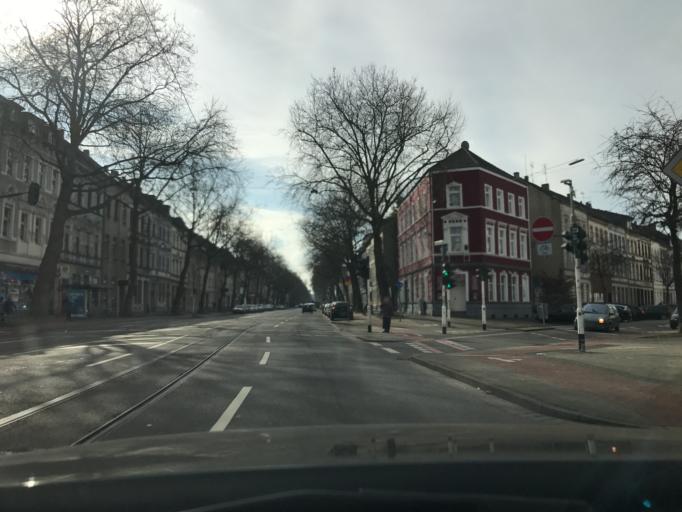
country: DE
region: North Rhine-Westphalia
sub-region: Regierungsbezirk Dusseldorf
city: Krefeld
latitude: 51.3208
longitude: 6.5624
